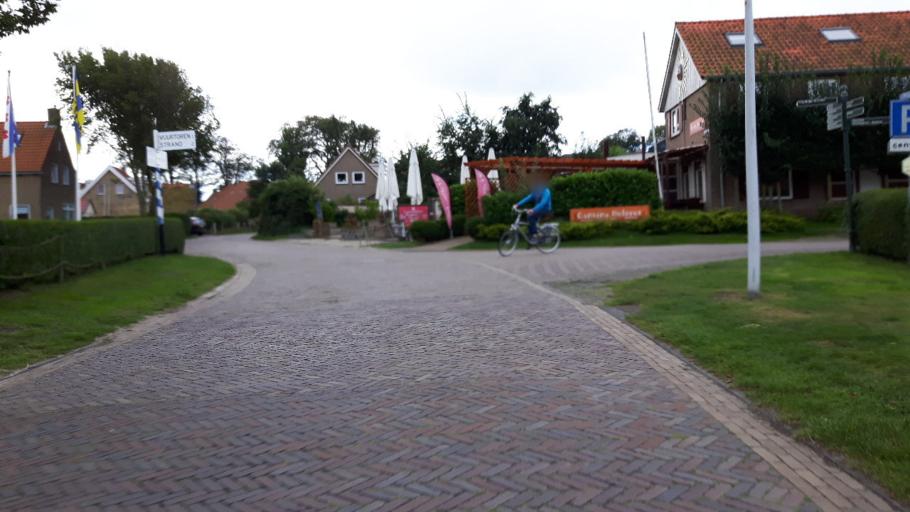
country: NL
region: Friesland
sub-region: Gemeente Ameland
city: Hollum
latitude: 53.4421
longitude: 5.6391
